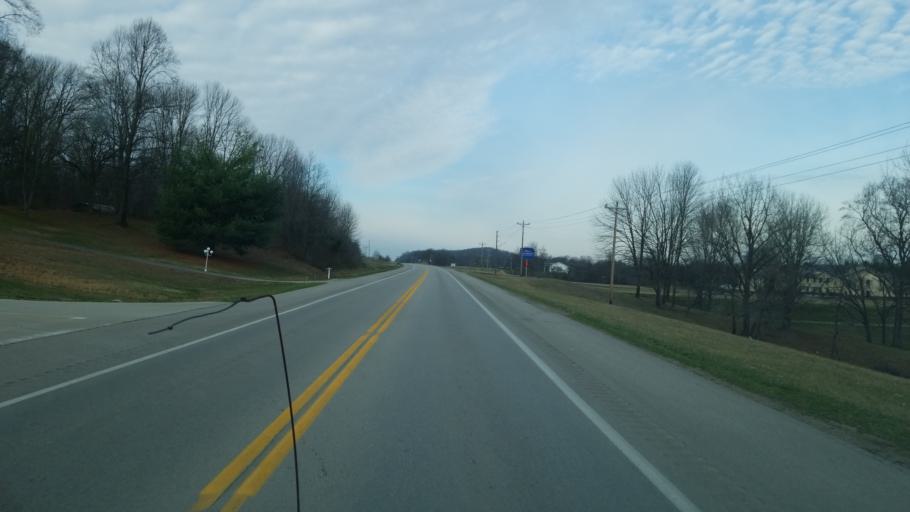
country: US
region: Kentucky
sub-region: Clinton County
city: Albany
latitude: 36.7548
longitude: -85.1413
